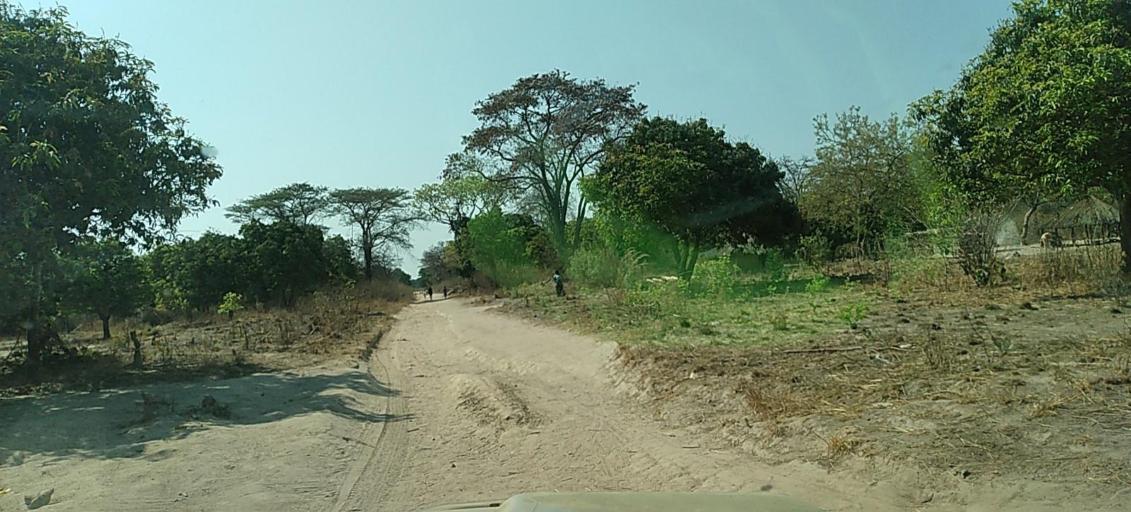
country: ZM
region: North-Western
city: Kalengwa
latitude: -13.3559
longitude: 24.8606
